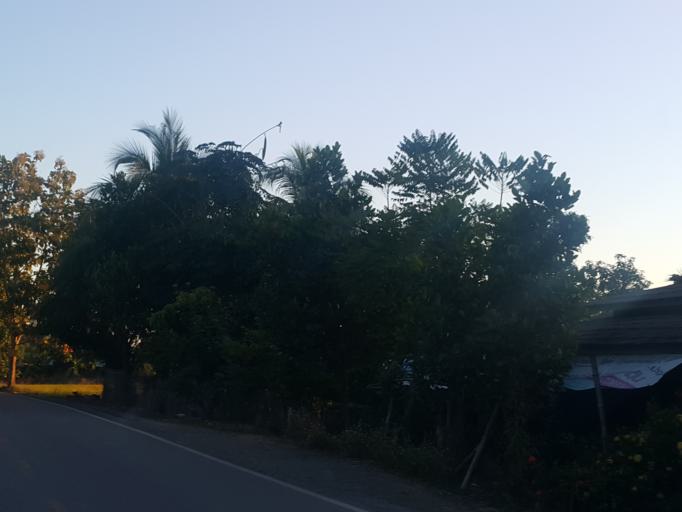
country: TH
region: Chiang Mai
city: San Sai
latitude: 18.8445
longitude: 99.1477
